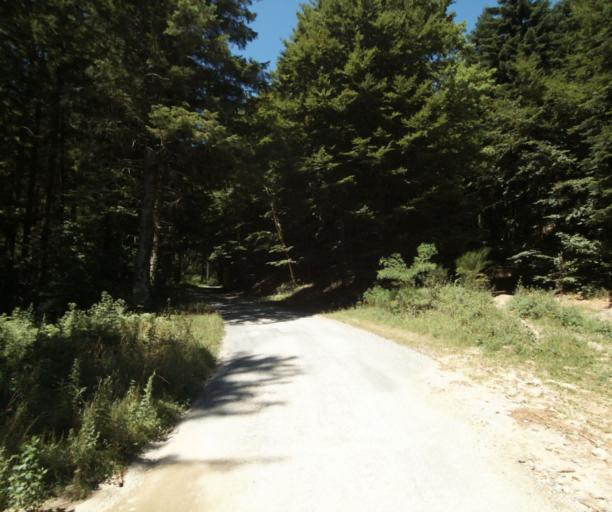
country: FR
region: Languedoc-Roussillon
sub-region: Departement de l'Aude
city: Cuxac-Cabardes
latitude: 43.4034
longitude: 2.2076
